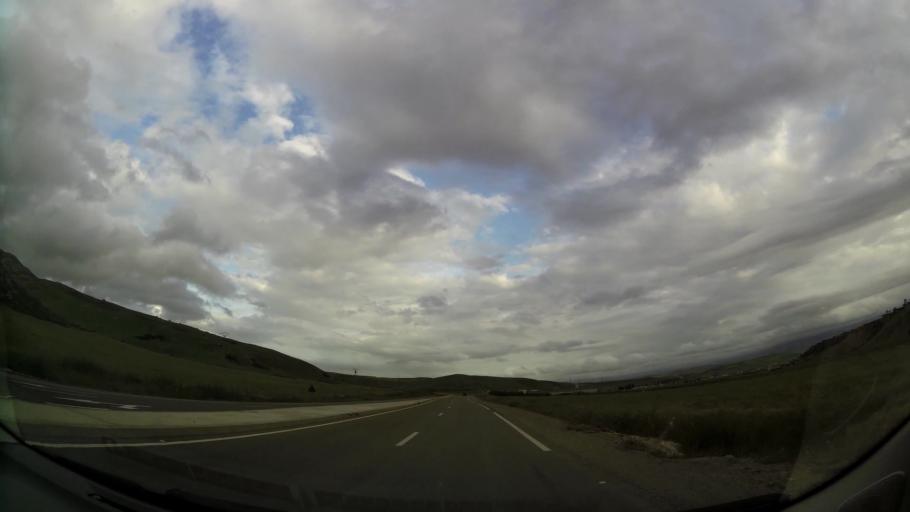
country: MA
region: Taza-Al Hoceima-Taounate
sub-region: Taza
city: Taza
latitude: 34.2864
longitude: -3.9619
